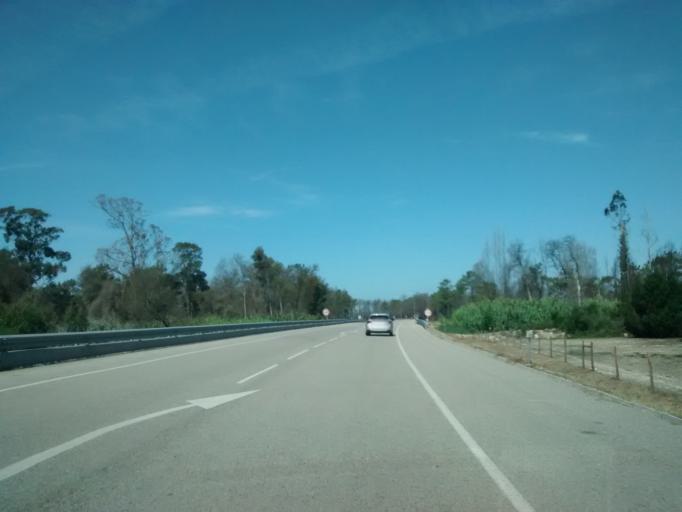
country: PT
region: Coimbra
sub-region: Mira
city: Mira
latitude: 40.4497
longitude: -8.7520
